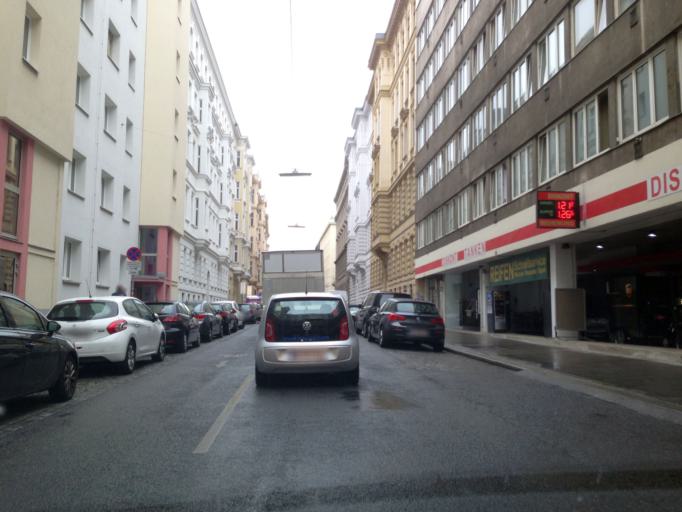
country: AT
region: Vienna
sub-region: Wien Stadt
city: Vienna
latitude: 48.1989
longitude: 16.3429
